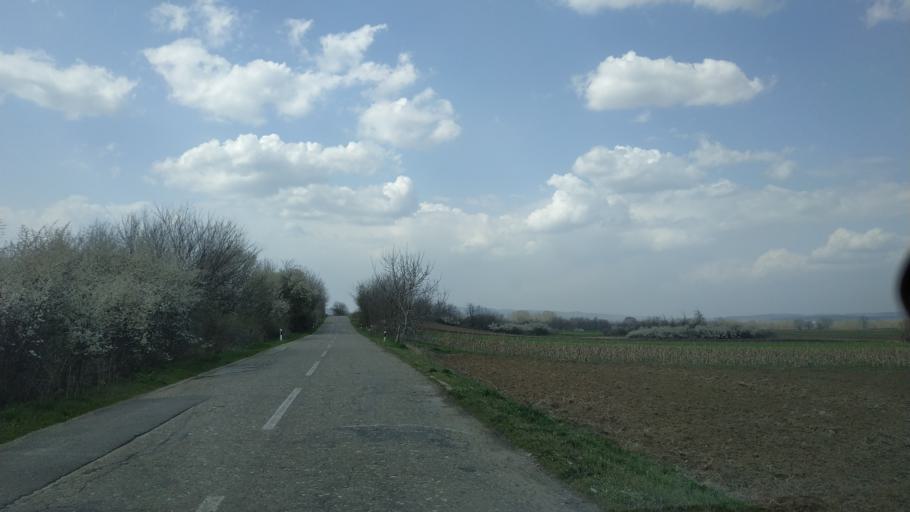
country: RS
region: Central Serbia
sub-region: Nisavski Okrug
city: Aleksinac
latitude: 43.5616
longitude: 21.6017
